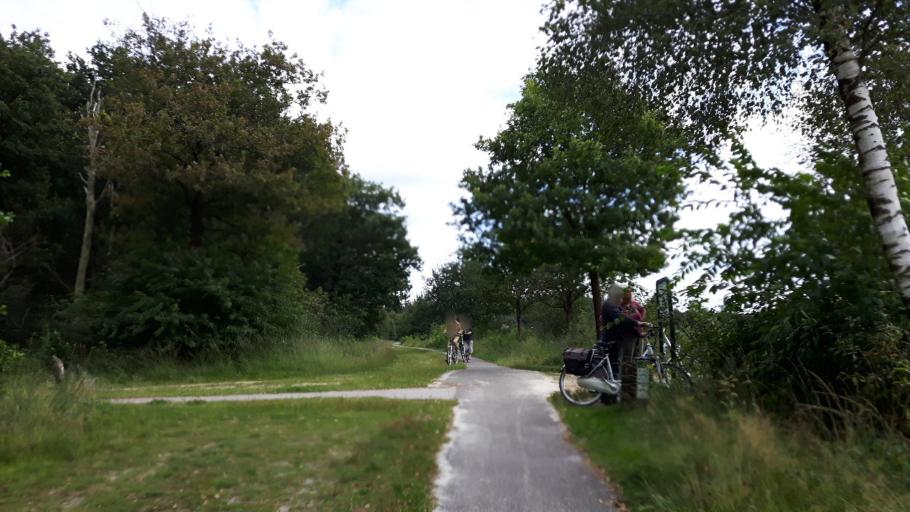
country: NL
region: Friesland
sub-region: Gemeente Smallingerland
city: Drachtstercompagnie
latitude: 53.0595
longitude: 6.2403
